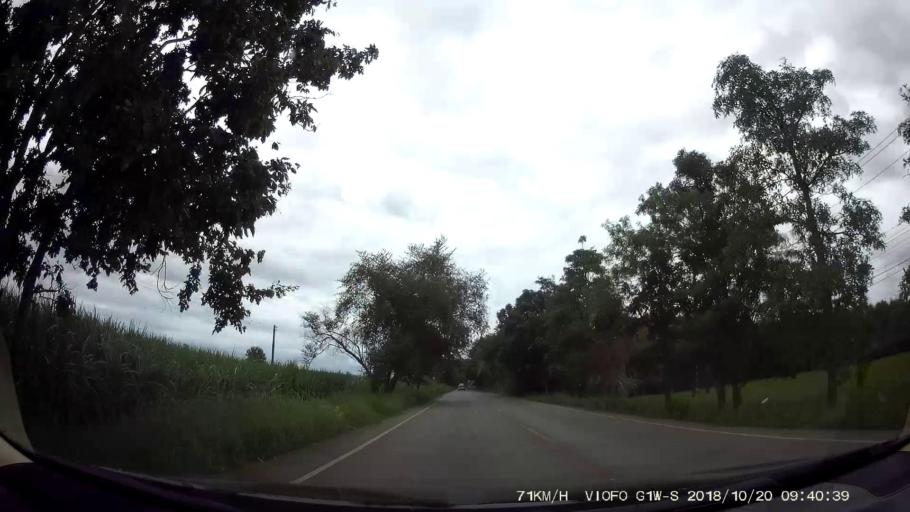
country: TH
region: Chaiyaphum
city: Kaset Sombun
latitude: 16.4451
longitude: 101.9605
